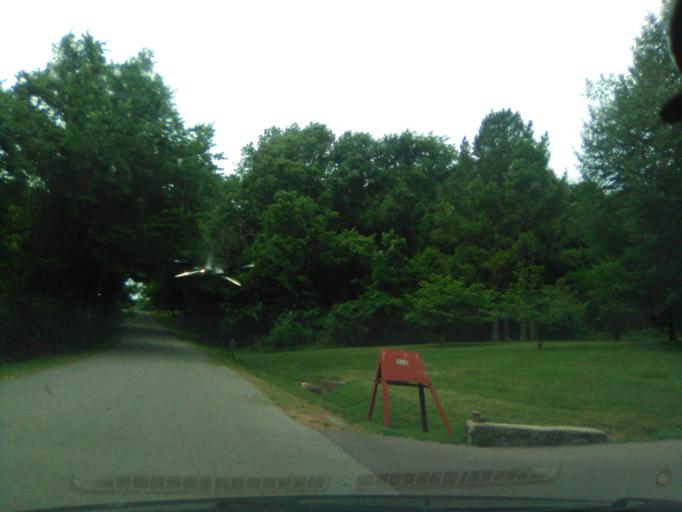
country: US
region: Tennessee
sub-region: Davidson County
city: Belle Meade
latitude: 36.0999
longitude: -86.8910
